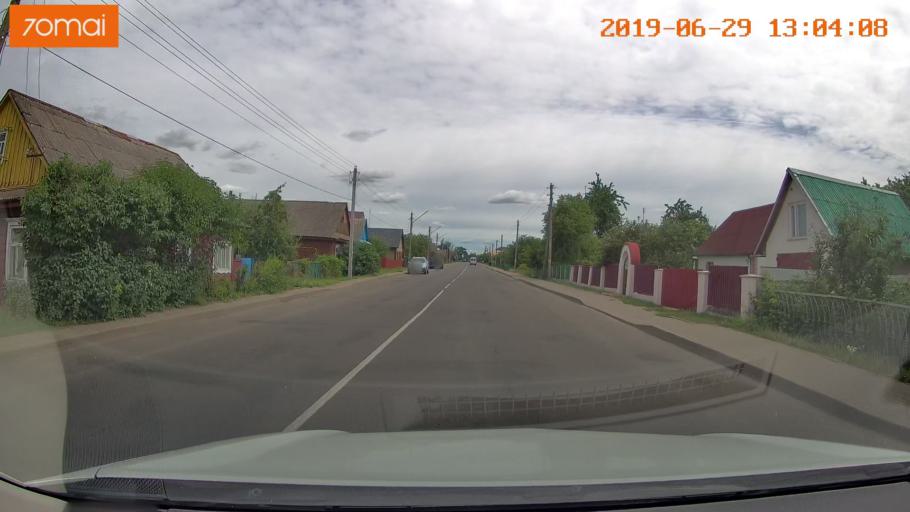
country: BY
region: Minsk
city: Slutsk
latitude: 53.0310
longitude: 27.5681
